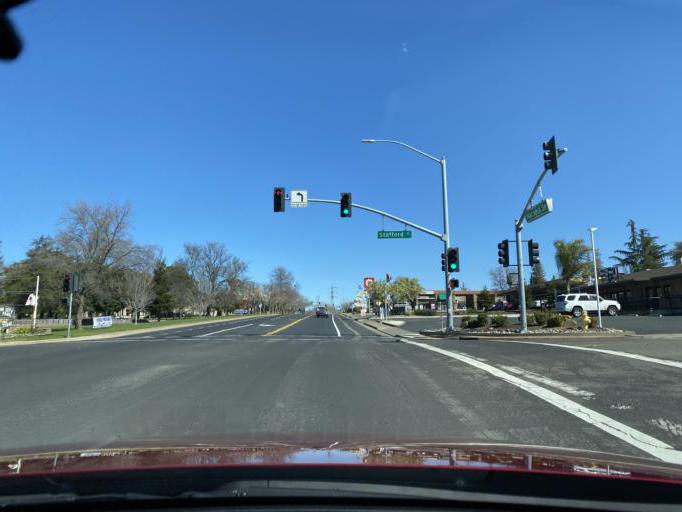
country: US
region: California
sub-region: Sacramento County
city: Folsom
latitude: 38.6798
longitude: -121.1664
